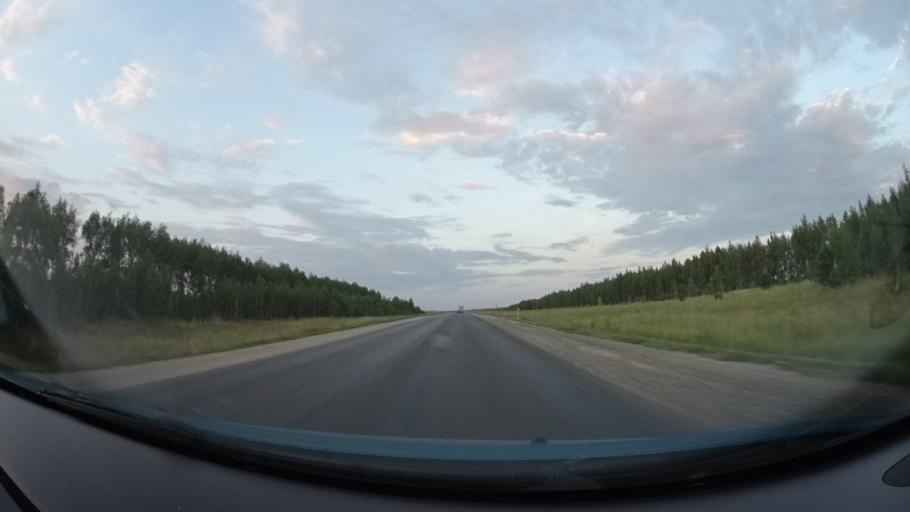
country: RU
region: Tatarstan
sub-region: Bugul'minskiy Rayon
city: Bugul'ma
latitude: 54.2575
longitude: 52.8896
